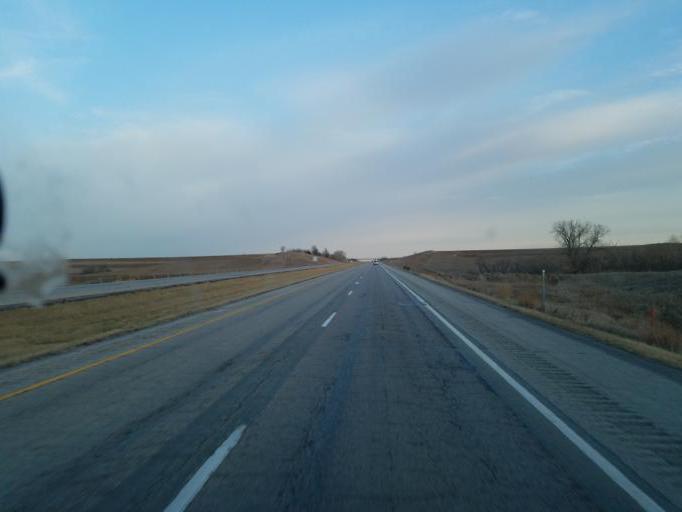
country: US
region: Iowa
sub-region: Harrison County
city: Missouri Valley
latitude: 41.4993
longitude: -95.7795
